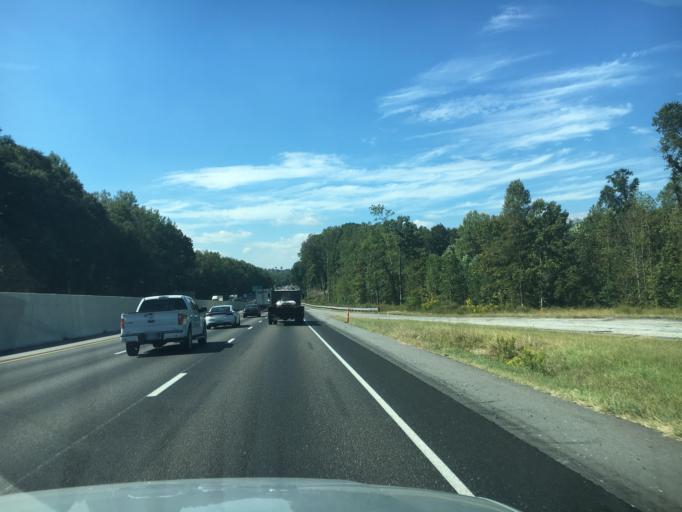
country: US
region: South Carolina
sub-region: Spartanburg County
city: Wellford
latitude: 34.9272
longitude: -82.0878
